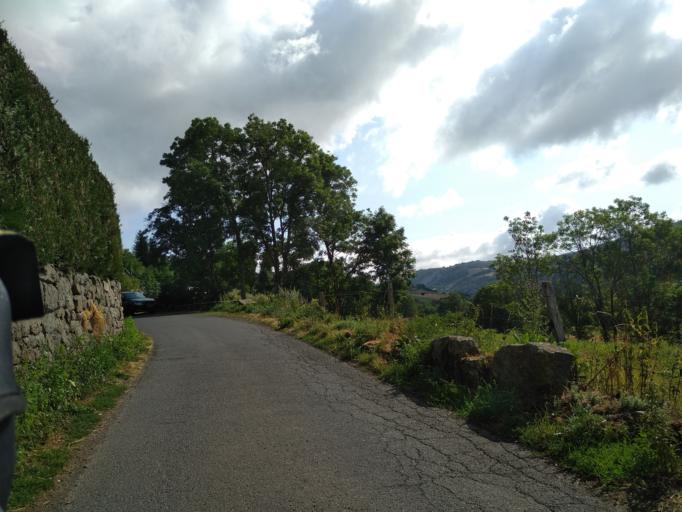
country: FR
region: Auvergne
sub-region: Departement du Cantal
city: Murat
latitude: 45.1375
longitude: 2.7476
